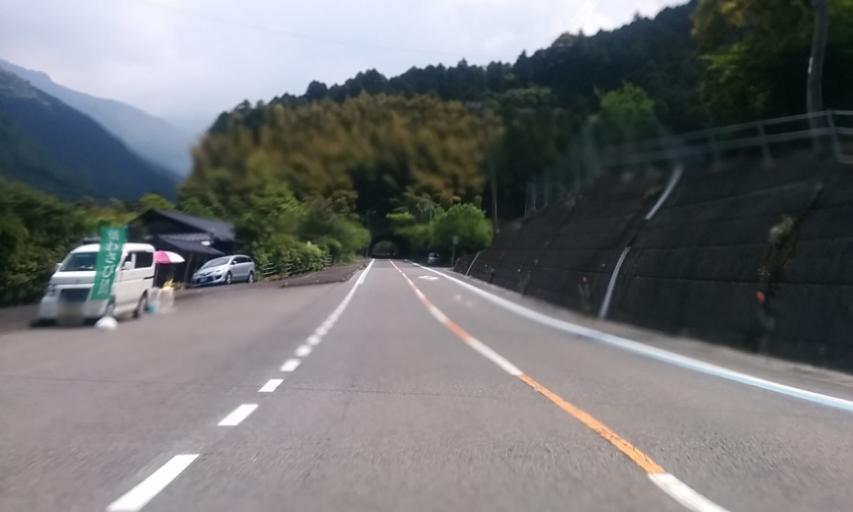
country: JP
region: Ehime
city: Saijo
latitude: 33.8469
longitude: 133.2159
